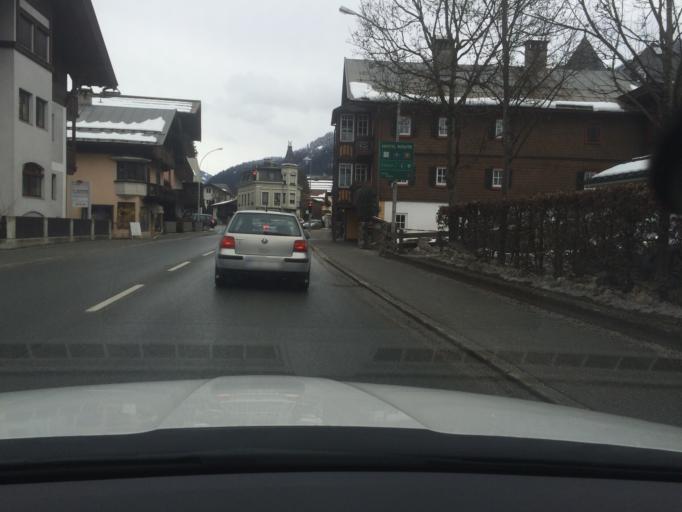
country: AT
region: Tyrol
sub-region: Politischer Bezirk Kitzbuhel
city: Kitzbuhel
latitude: 47.4512
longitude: 12.3896
